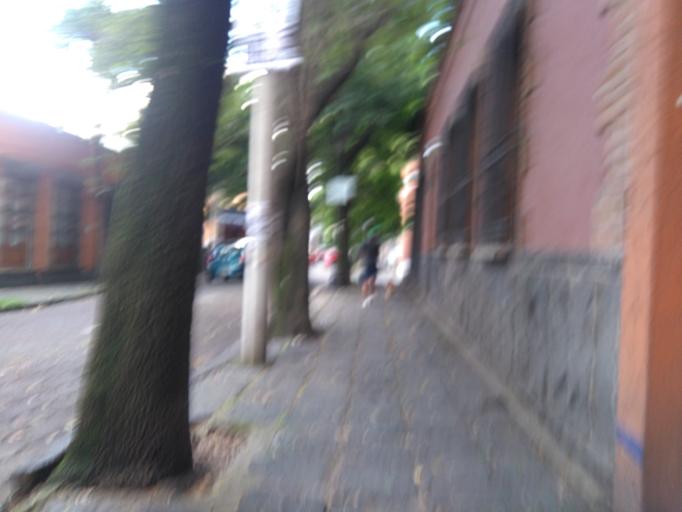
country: MX
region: Mexico City
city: Coyoacan
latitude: 19.3495
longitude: -99.1731
